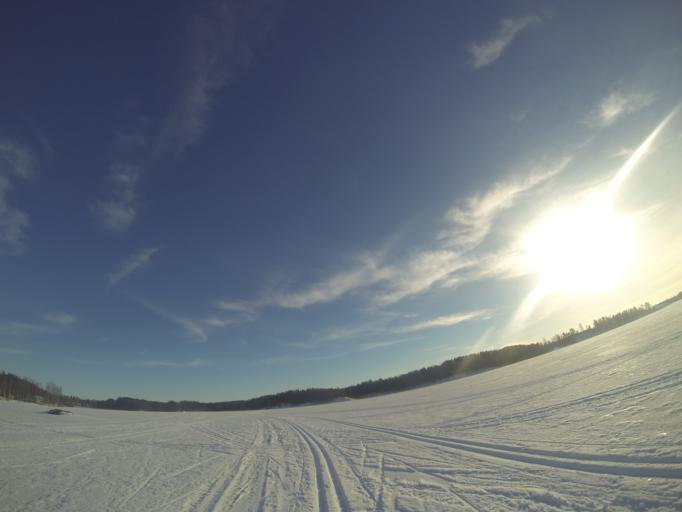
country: FI
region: Southern Savonia
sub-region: Savonlinna
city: Savonlinna
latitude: 61.8825
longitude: 28.9080
